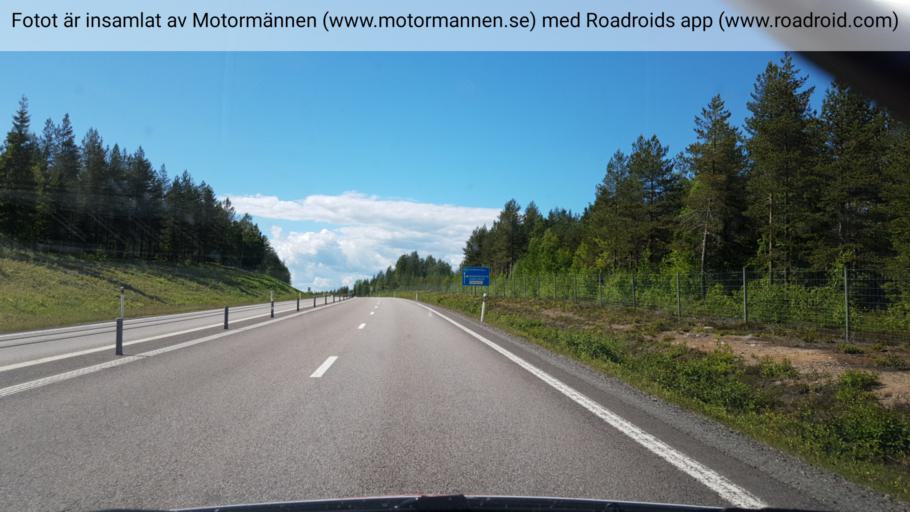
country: SE
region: Norrbotten
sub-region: Kalix Kommun
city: Toere
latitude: 65.9174
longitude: 22.7718
